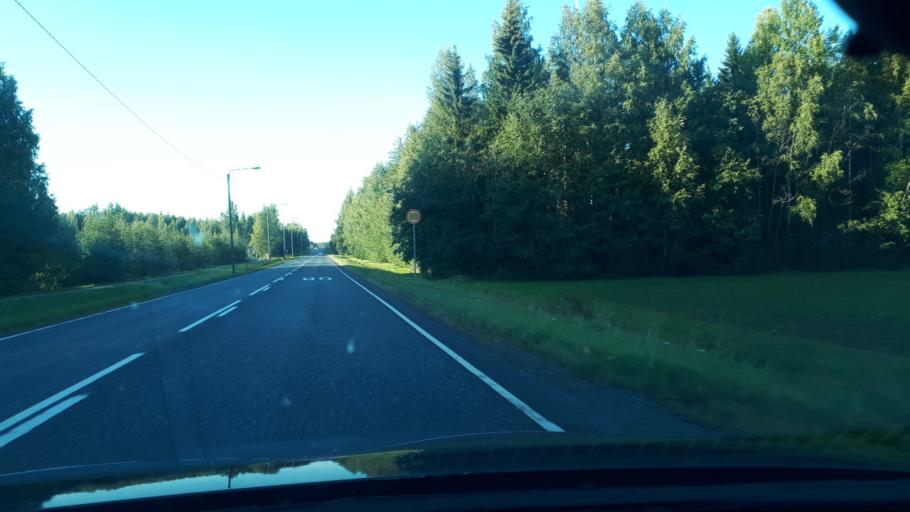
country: FI
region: Northern Savo
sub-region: Ylae-Savo
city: Lapinlahti
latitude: 63.4262
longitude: 27.3294
